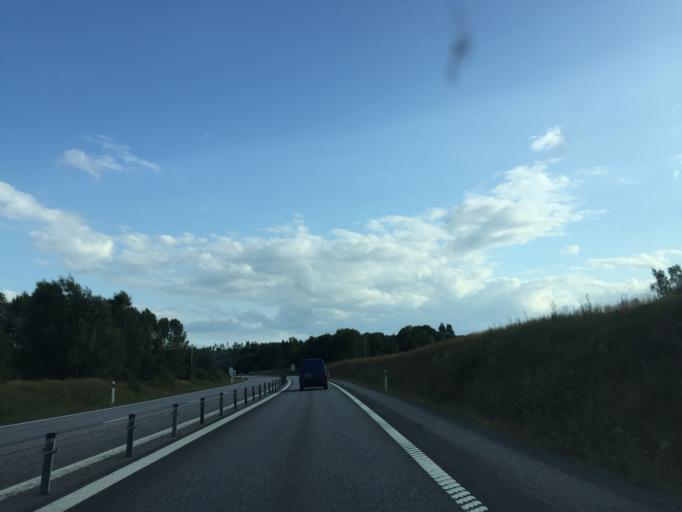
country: SE
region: OEstergoetland
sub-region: Motala Kommun
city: Motala
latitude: 58.6228
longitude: 14.9800
